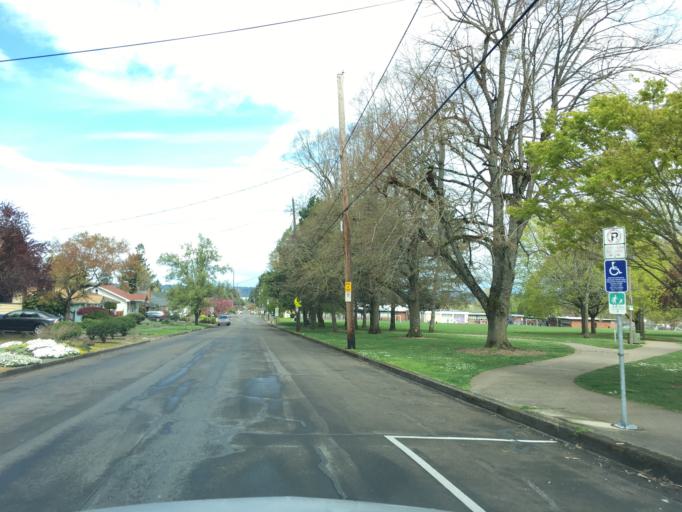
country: US
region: Oregon
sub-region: Multnomah County
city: Lents
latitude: 45.5526
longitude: -122.5953
